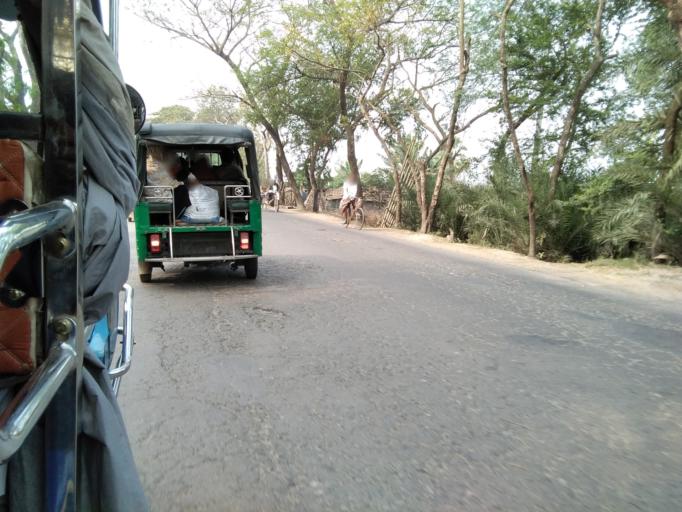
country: BD
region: Khulna
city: Satkhira
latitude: 22.6901
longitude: 89.0366
